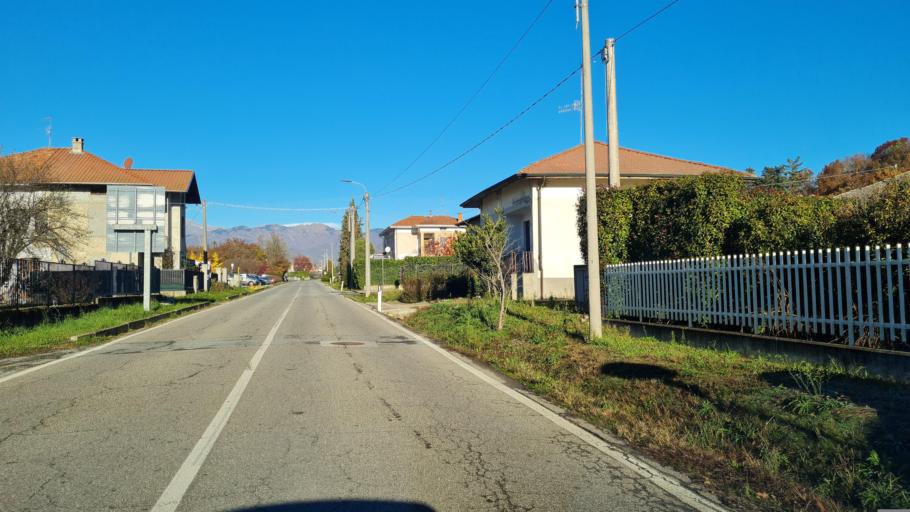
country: IT
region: Piedmont
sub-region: Provincia di Biella
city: Cossato
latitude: 45.5542
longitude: 8.2057
